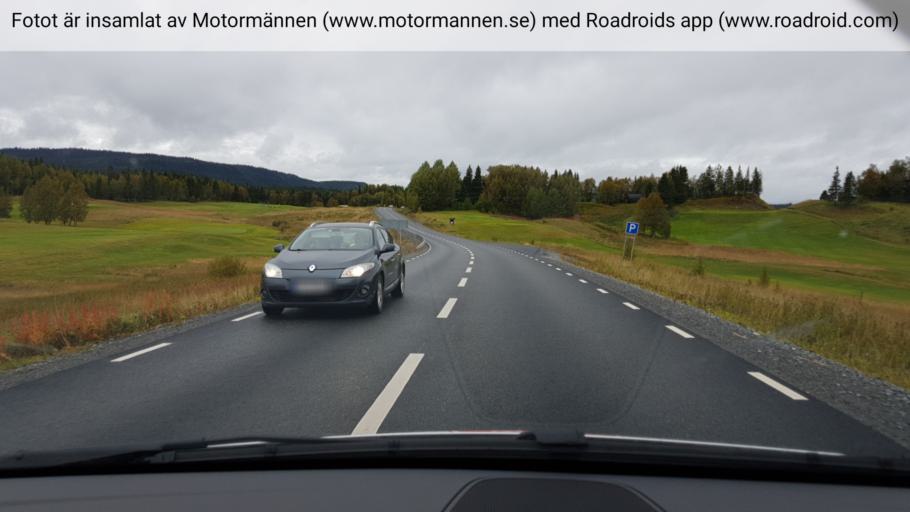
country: SE
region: Jaemtland
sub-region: Are Kommun
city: Are
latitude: 63.4017
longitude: 12.8240
